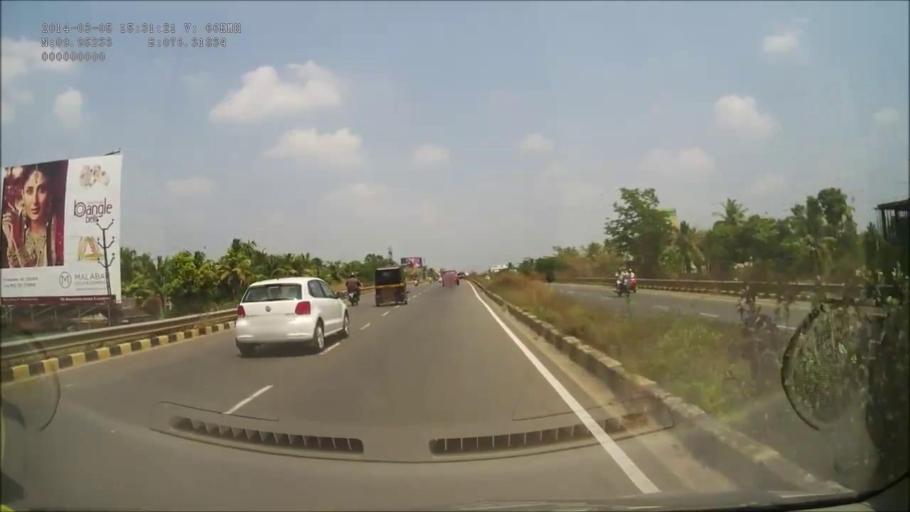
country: IN
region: Kerala
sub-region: Ernakulam
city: Cochin
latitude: 9.9528
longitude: 76.3183
